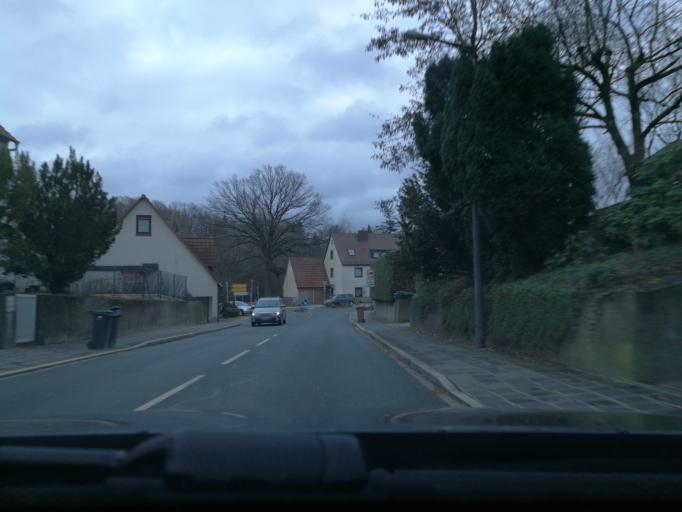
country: DE
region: Bavaria
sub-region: Regierungsbezirk Mittelfranken
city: Heroldsberg
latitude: 49.5395
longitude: 11.1553
